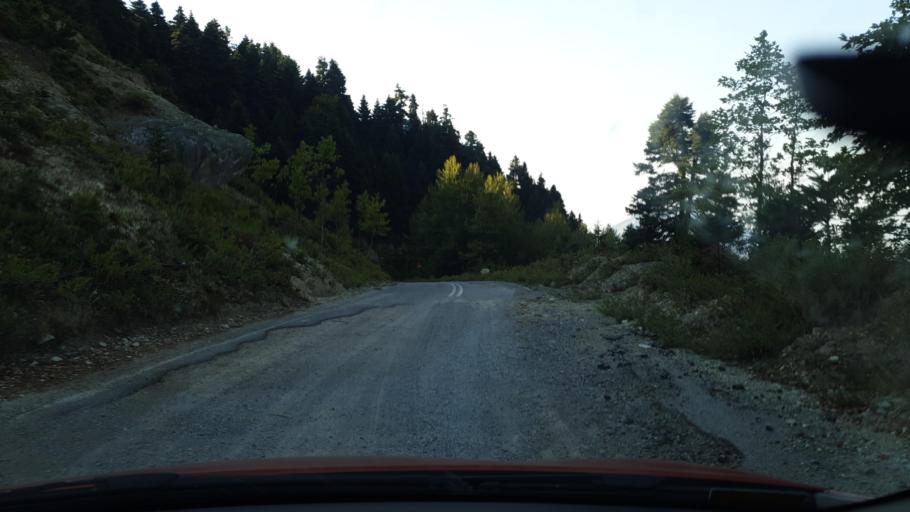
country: GR
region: Central Greece
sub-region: Nomos Evvoias
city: Yimnon
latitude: 38.5968
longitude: 23.9023
